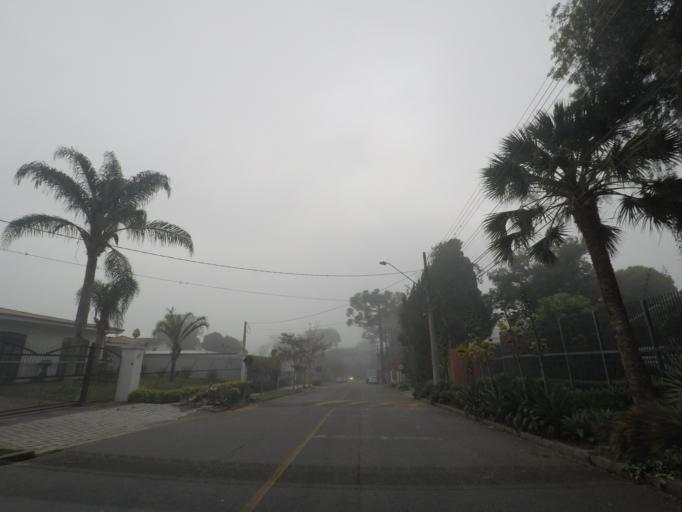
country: BR
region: Parana
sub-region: Curitiba
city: Curitiba
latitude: -25.4434
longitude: -49.2937
